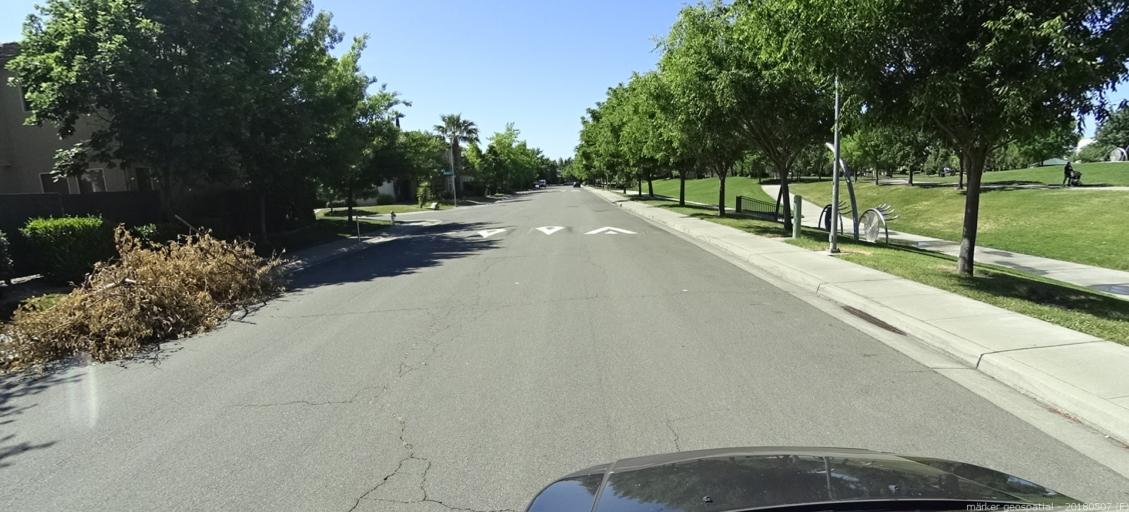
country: US
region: California
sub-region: Sacramento County
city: Rio Linda
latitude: 38.6614
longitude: -121.5006
